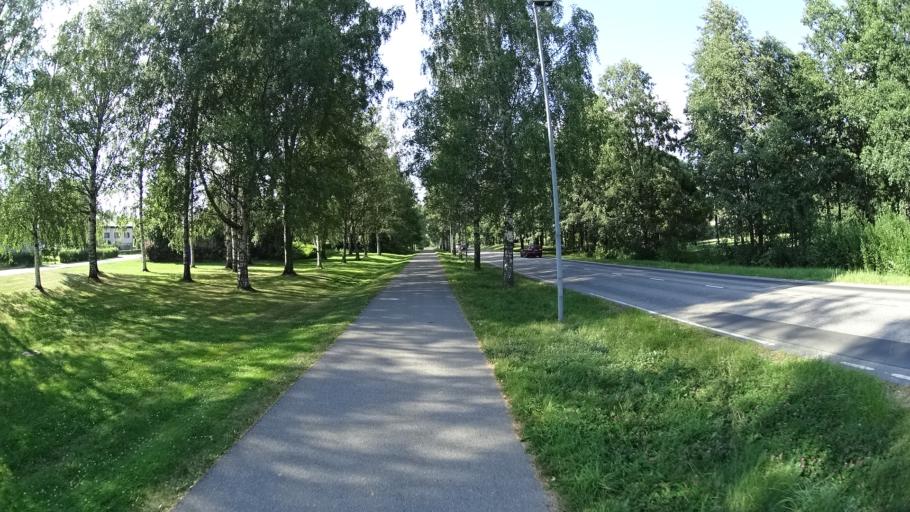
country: FI
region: Uusimaa
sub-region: Porvoo
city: Porvoo
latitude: 60.4019
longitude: 25.6706
